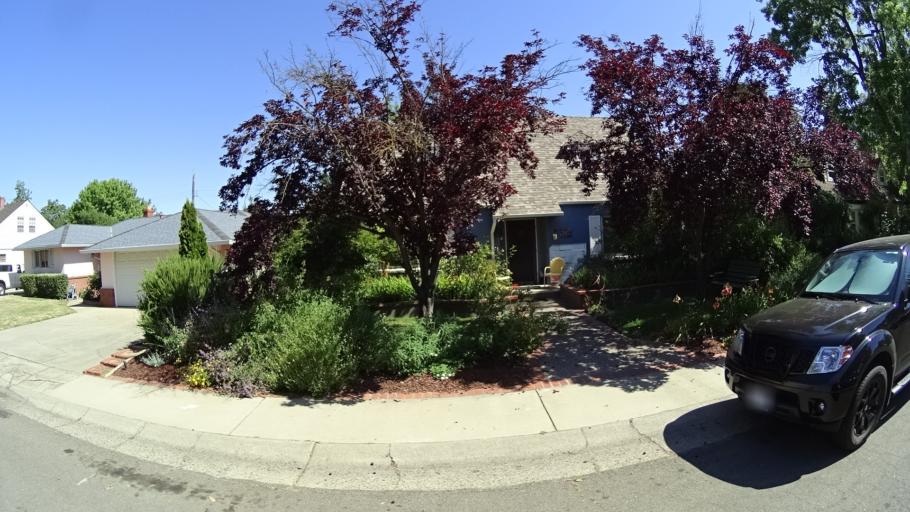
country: US
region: California
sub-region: Sacramento County
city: Parkway
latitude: 38.5263
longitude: -121.5034
